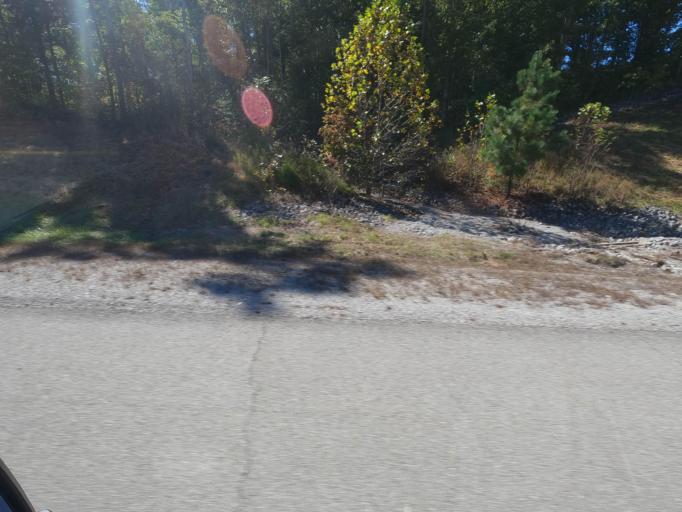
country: US
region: Tennessee
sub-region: Williamson County
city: Fairview
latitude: 35.8884
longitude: -87.1152
